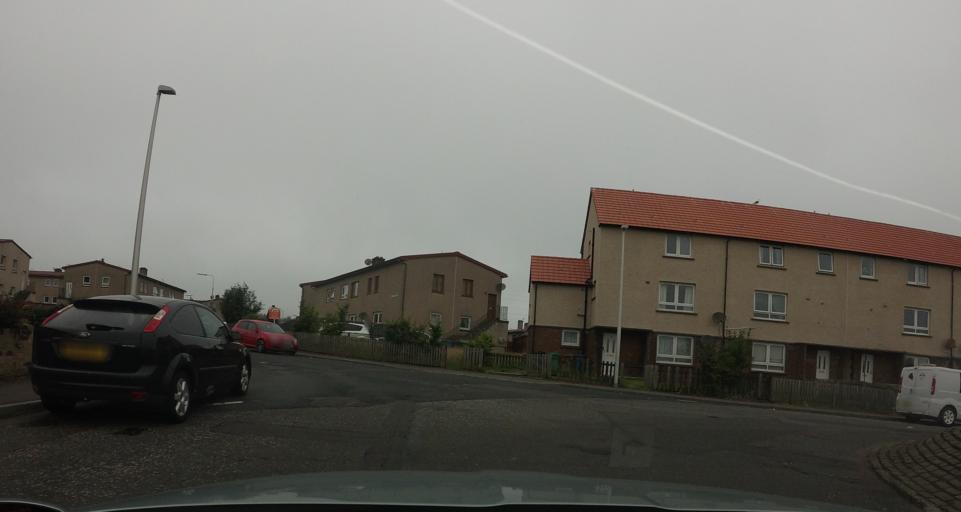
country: GB
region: Scotland
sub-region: Fife
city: Kelty
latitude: 56.1325
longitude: -3.3895
